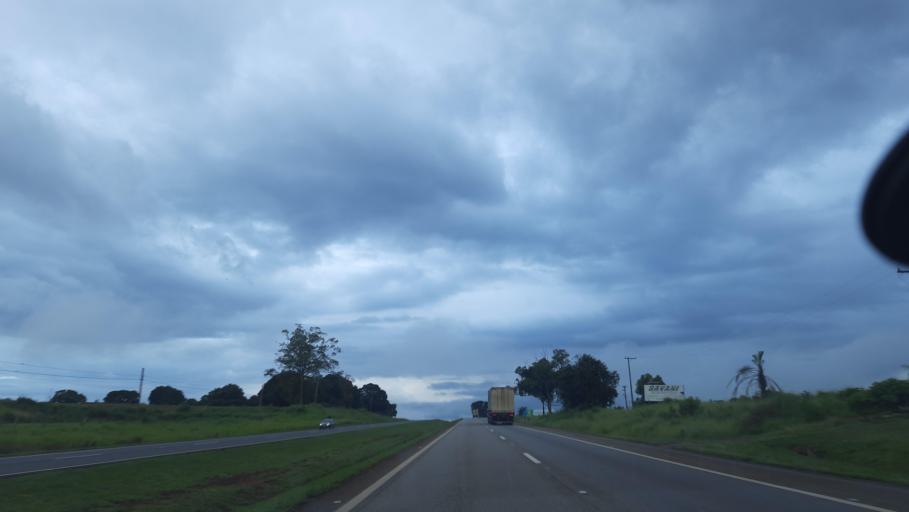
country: BR
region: Sao Paulo
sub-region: Moji-Guacu
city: Mogi-Gaucu
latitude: -22.2506
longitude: -46.9777
